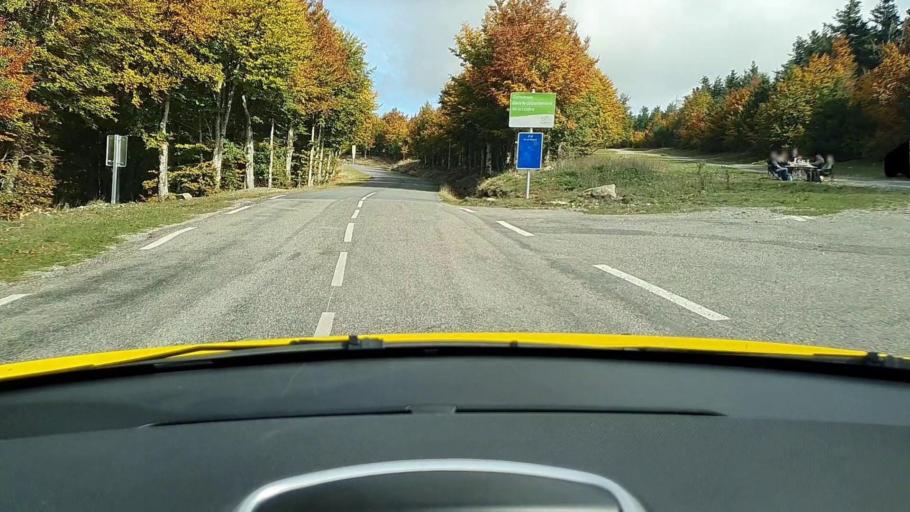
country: FR
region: Languedoc-Roussillon
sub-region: Departement du Gard
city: Valleraugue
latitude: 44.1192
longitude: 3.5584
